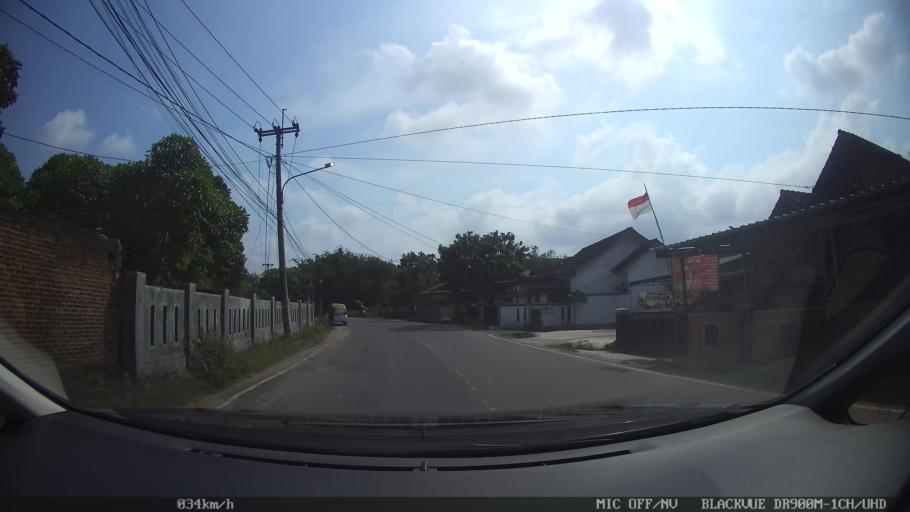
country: ID
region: Lampung
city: Kedaton
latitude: -5.3541
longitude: 105.2631
